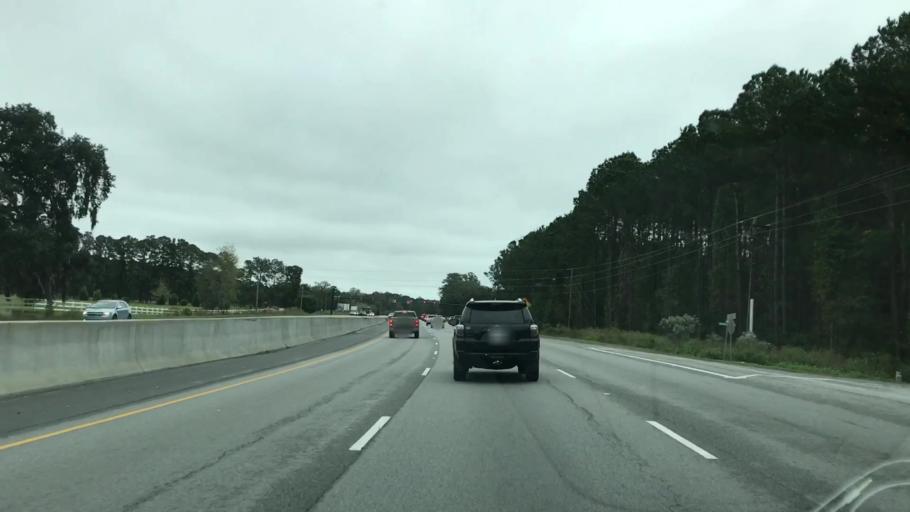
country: US
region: South Carolina
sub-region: Beaufort County
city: Bluffton
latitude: 32.2891
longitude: -80.9272
